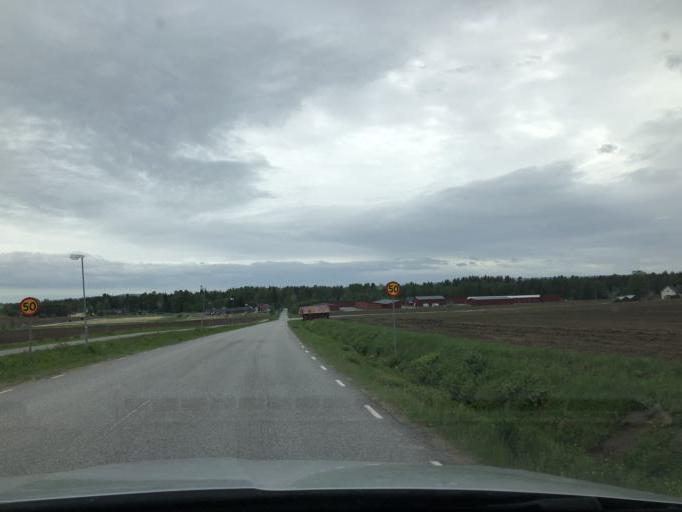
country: SE
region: Norrbotten
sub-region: Pitea Kommun
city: Bergsviken
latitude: 65.3828
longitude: 21.3138
